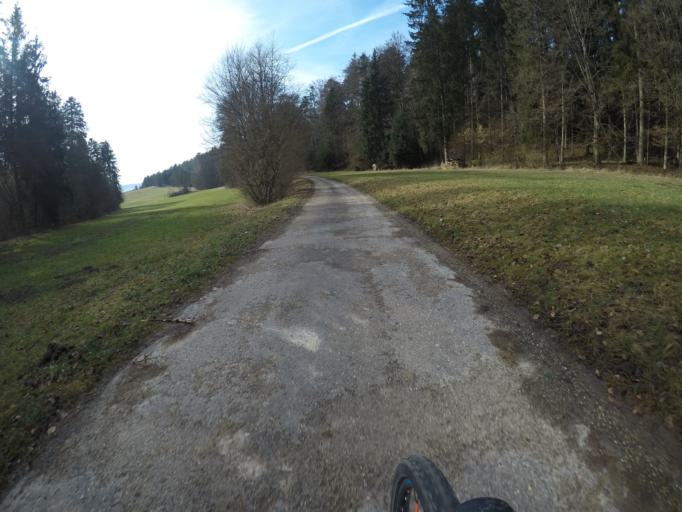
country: DE
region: Baden-Wuerttemberg
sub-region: Karlsruhe Region
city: Wildberg
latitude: 48.6687
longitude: 8.7734
